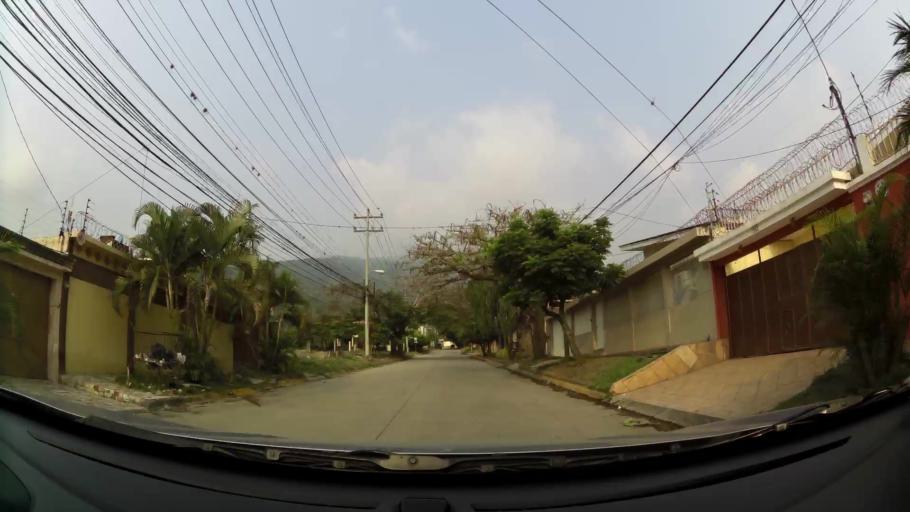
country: HN
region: Cortes
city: Armenta
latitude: 15.4827
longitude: -88.0392
